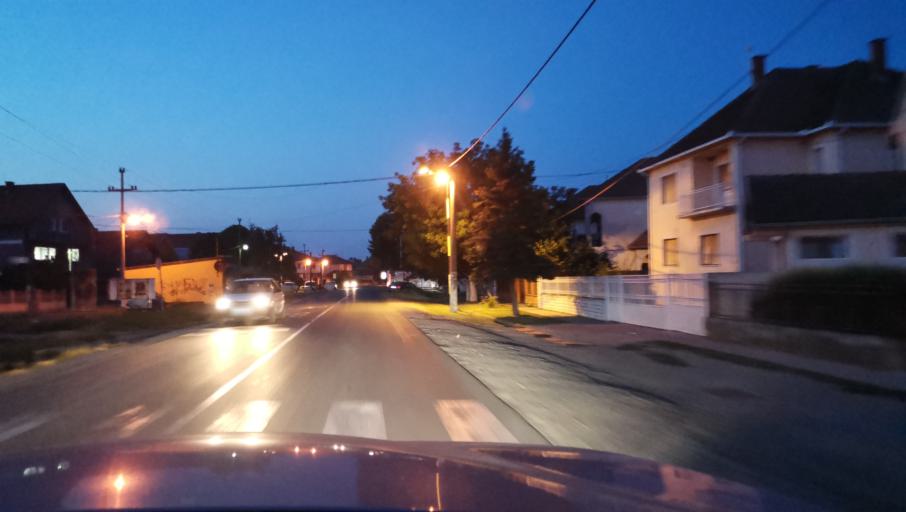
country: RS
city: Boljevci
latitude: 44.7508
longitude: 20.2566
